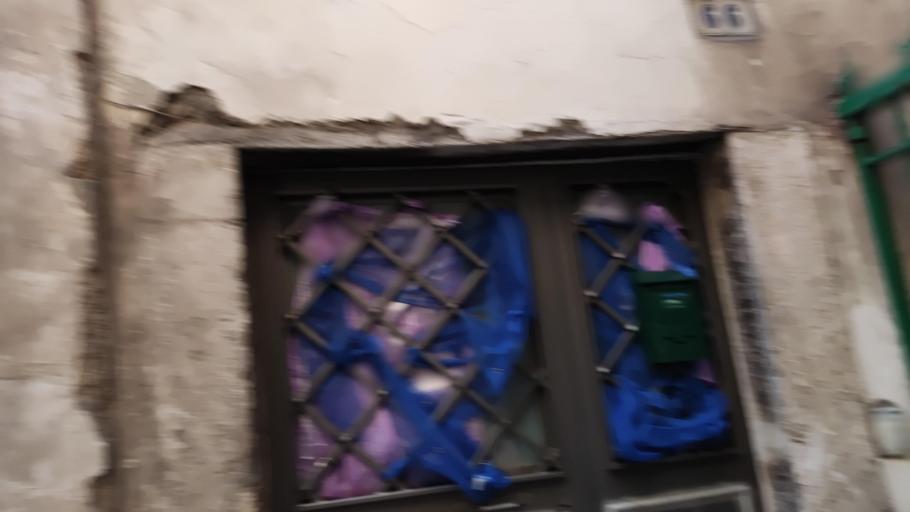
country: IT
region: Latium
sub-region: Citta metropolitana di Roma Capitale
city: Tivoli
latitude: 41.9659
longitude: 12.7983
